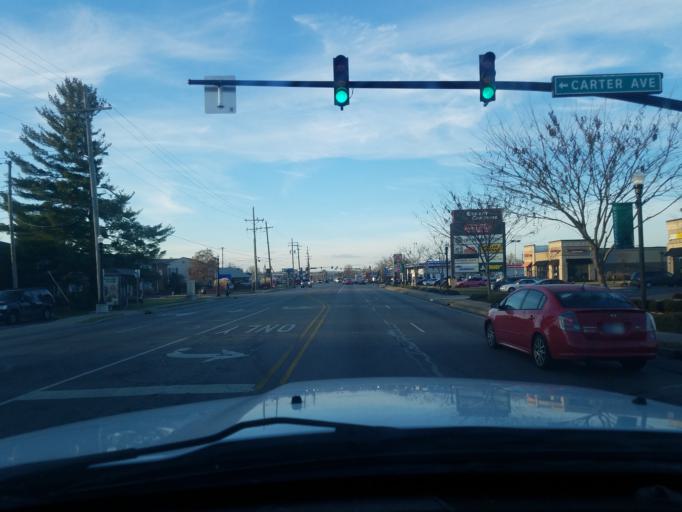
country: US
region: Indiana
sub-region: Clark County
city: Clarksville
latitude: 38.3002
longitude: -85.7623
